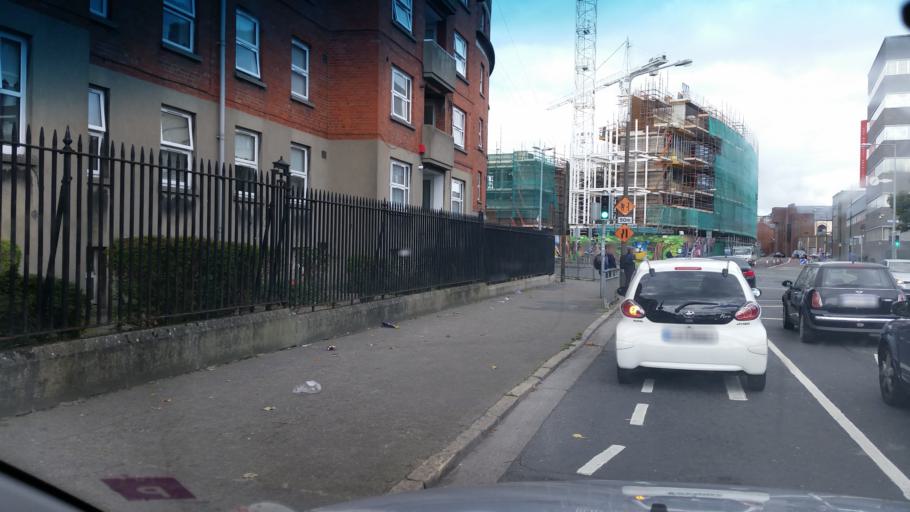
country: IE
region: Leinster
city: Rathmines
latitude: 53.3377
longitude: -6.2692
